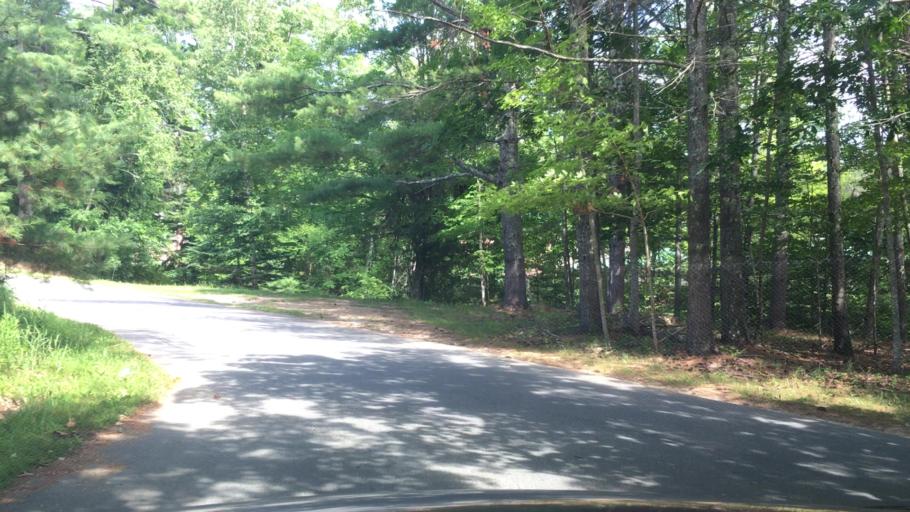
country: US
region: Maine
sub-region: Hancock County
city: Orland
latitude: 44.5856
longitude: -68.6905
